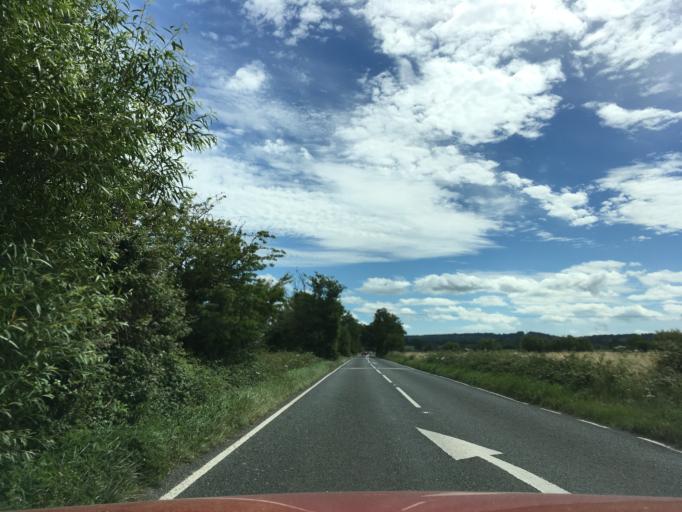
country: GB
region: England
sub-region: Somerset
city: Glastonbury
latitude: 51.1330
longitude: -2.7128
